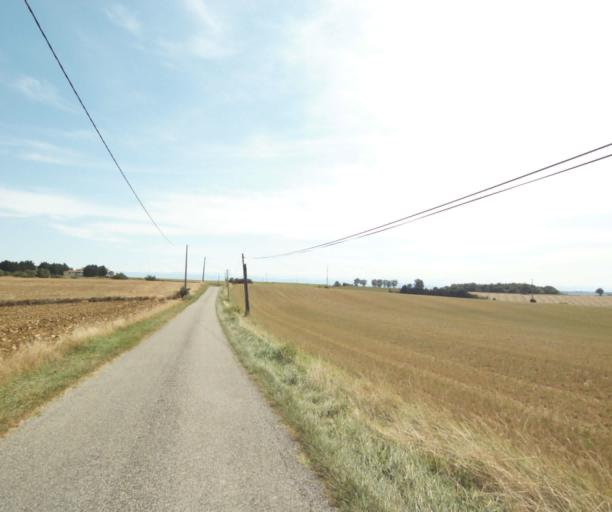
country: FR
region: Midi-Pyrenees
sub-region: Departement de la Haute-Garonne
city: Gaillac-Toulza
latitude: 43.2506
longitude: 1.4189
